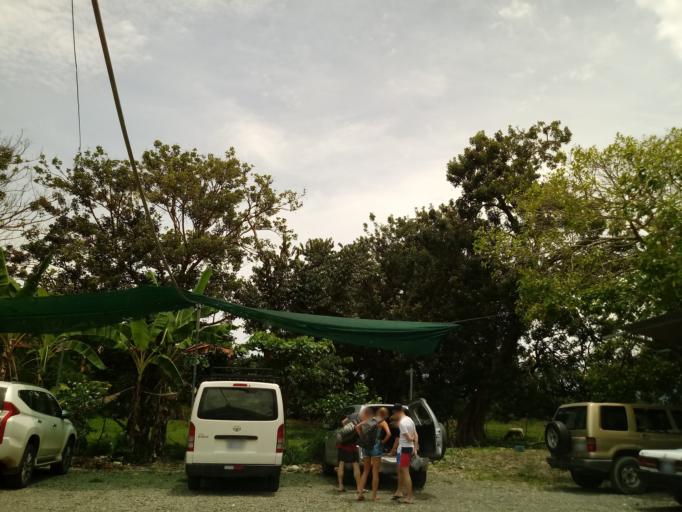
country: CR
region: San Jose
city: Daniel Flores
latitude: 9.1558
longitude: -83.7480
